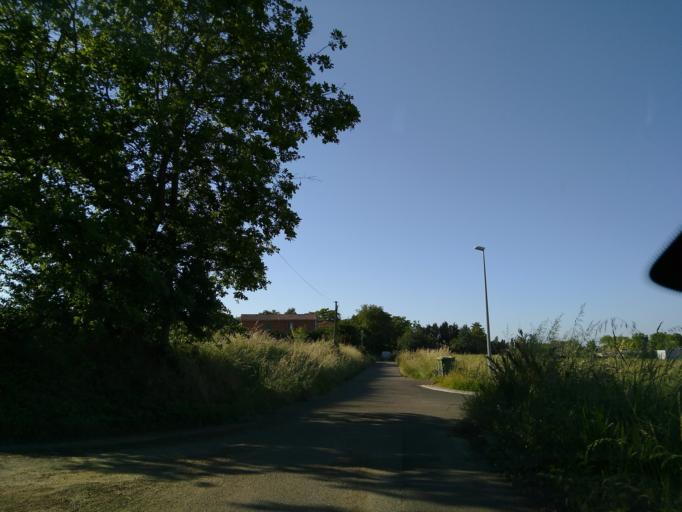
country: FR
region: Midi-Pyrenees
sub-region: Departement de la Haute-Garonne
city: Grenade
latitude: 43.7548
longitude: 1.2994
